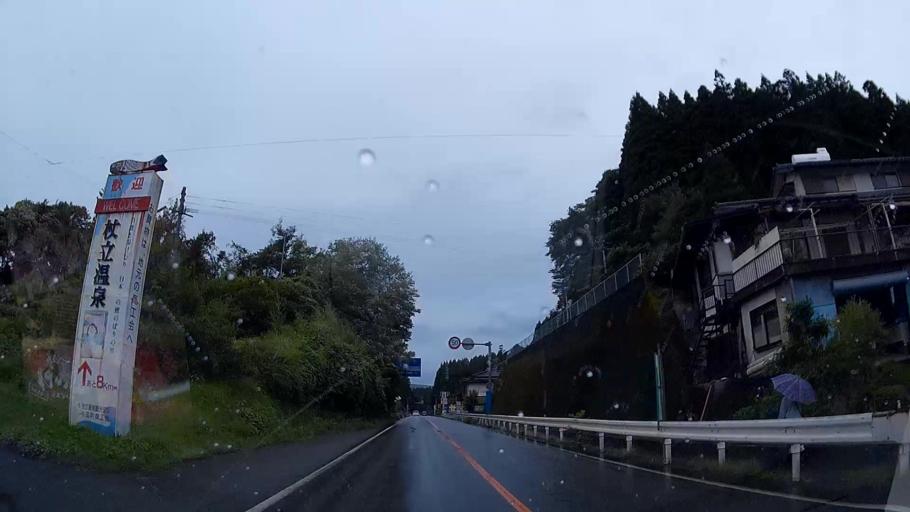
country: JP
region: Oita
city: Tsukawaki
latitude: 33.1290
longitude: 131.0630
